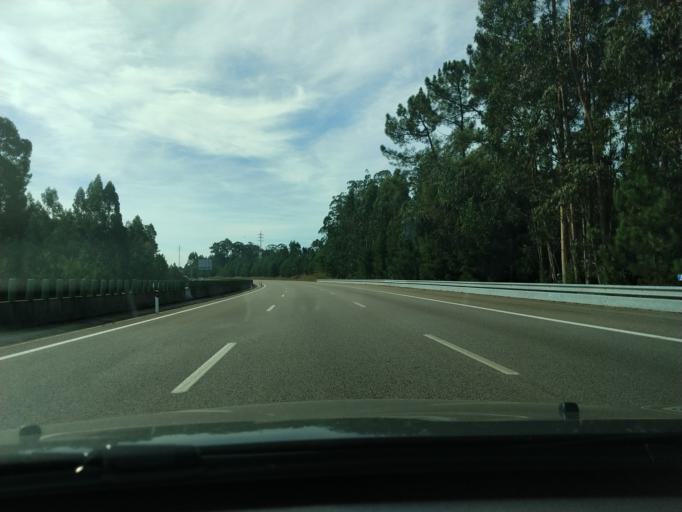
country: PT
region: Aveiro
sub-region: Ovar
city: Valega
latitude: 40.8510
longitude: -8.5569
